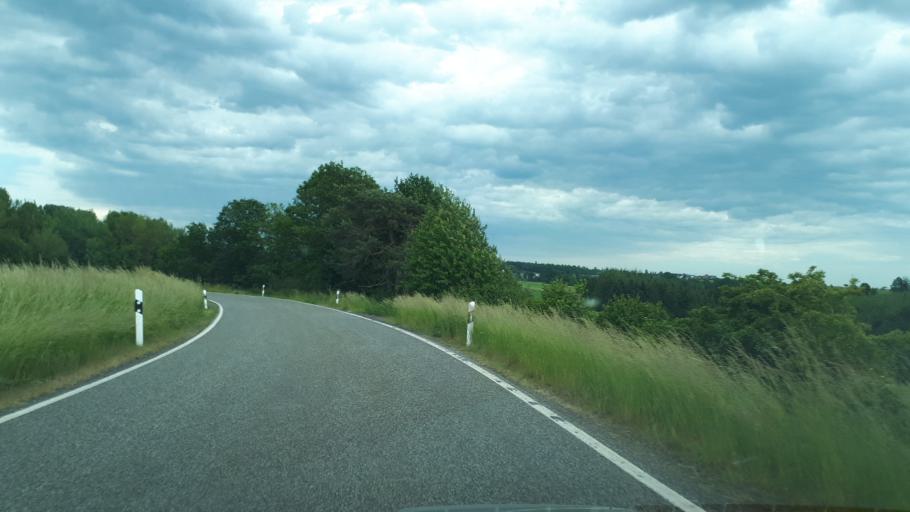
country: DE
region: Rheinland-Pfalz
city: Auderath
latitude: 50.1777
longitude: 6.9904
